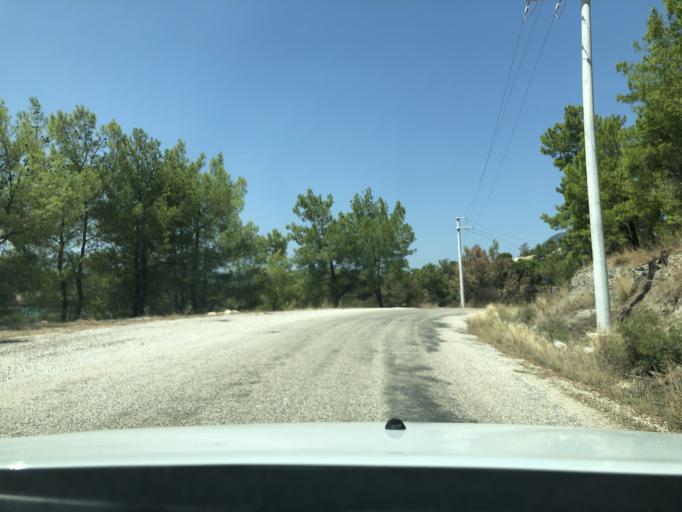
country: TR
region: Antalya
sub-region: Manavgat
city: Kizilagac
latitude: 36.8660
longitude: 31.5585
